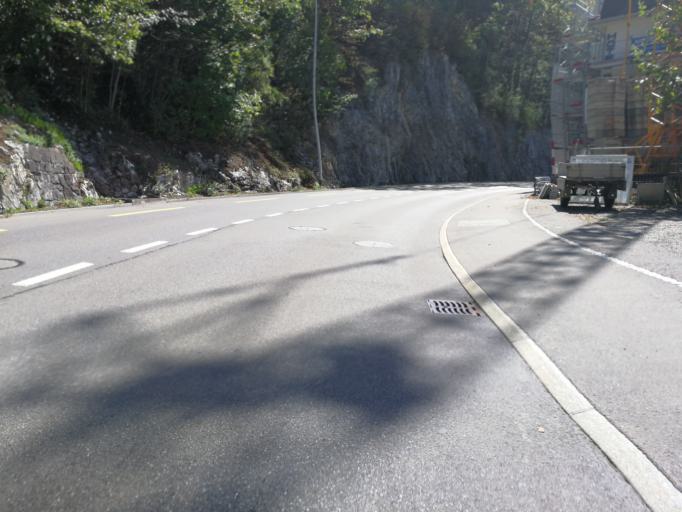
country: CH
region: Schwyz
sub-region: Bezirk Gersau
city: Gersau
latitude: 46.9898
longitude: 8.5326
